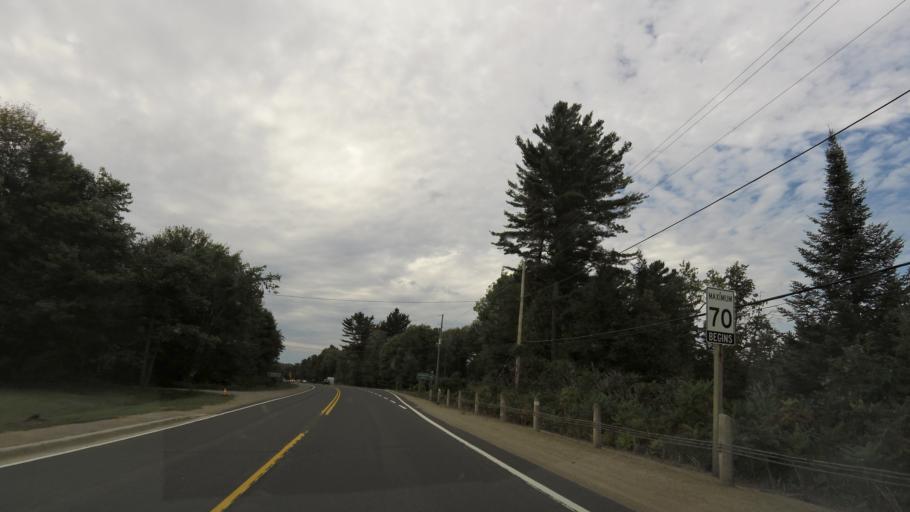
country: CA
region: Ontario
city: Omemee
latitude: 44.7321
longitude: -78.8203
